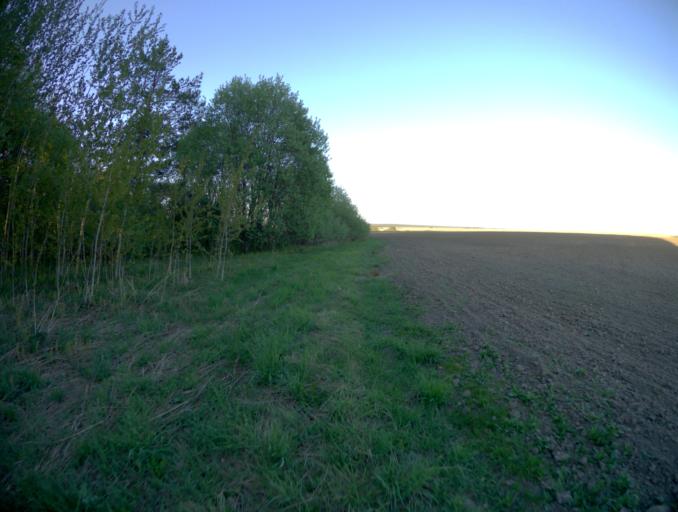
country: RU
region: Ivanovo
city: Gavrilov Posad
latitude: 56.4261
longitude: 40.2017
